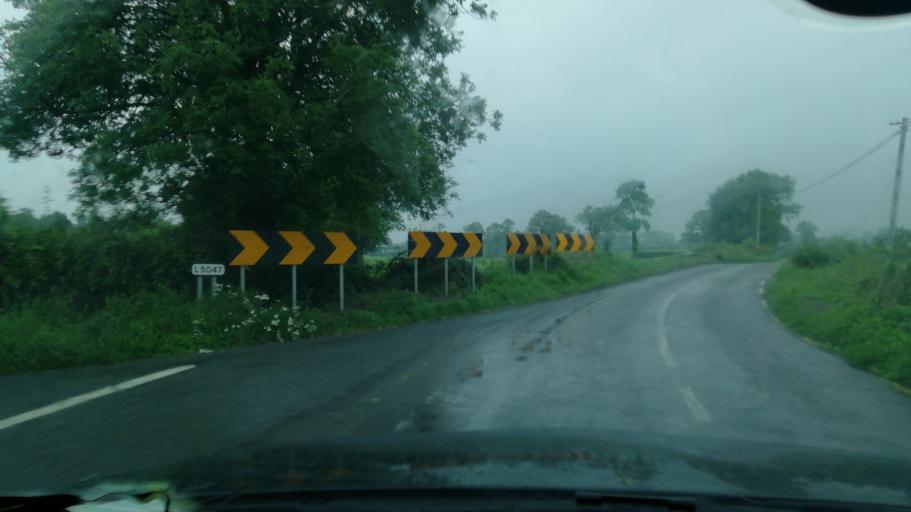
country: IE
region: Leinster
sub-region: Kilkenny
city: Kilkenny
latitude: 52.5690
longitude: -7.2792
